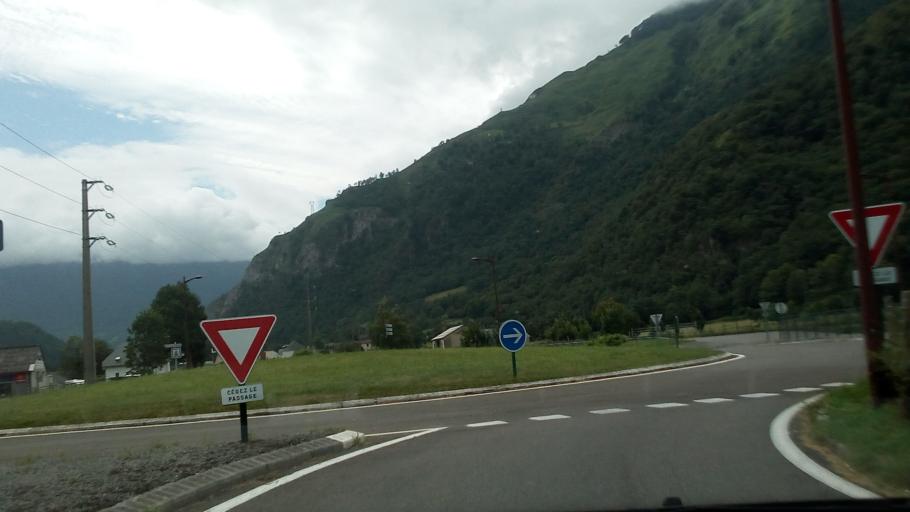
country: FR
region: Aquitaine
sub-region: Departement des Pyrenees-Atlantiques
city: Laruns
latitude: 43.0243
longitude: -0.4217
